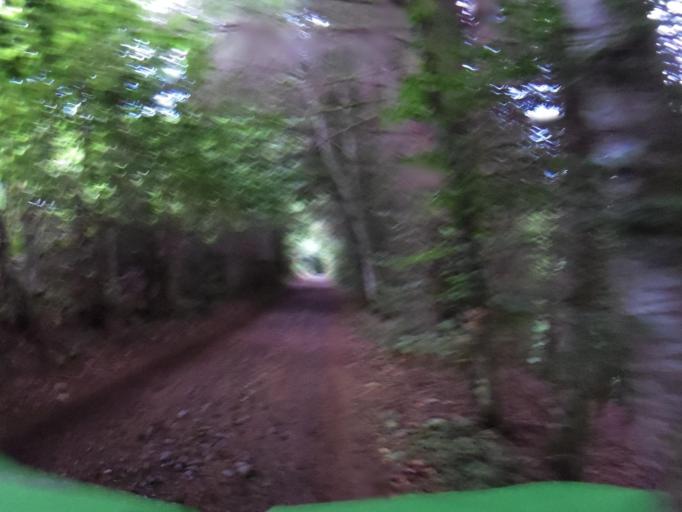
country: BE
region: Wallonia
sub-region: Province de Namur
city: Bievre
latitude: 49.8681
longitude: 4.9925
